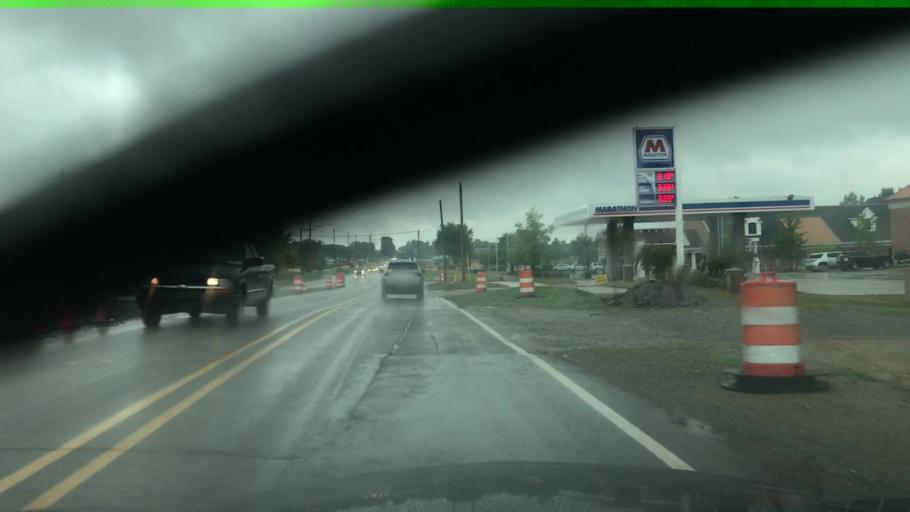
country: US
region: Michigan
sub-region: Oakland County
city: Auburn Hills
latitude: 42.7230
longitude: -83.3074
